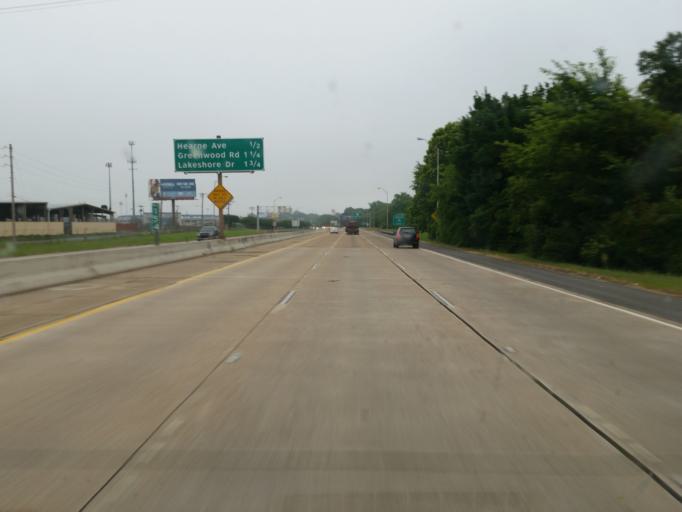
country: US
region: Louisiana
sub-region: Caddo Parish
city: Shreveport
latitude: 32.4739
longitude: -93.7910
